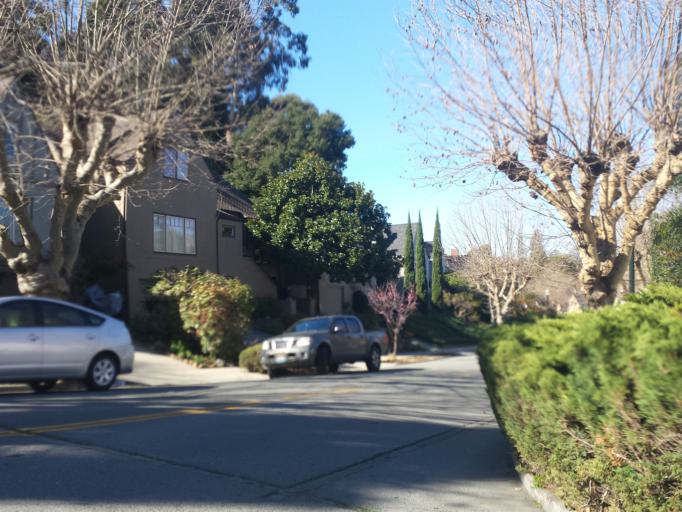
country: US
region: California
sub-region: Alameda County
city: Piedmont
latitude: 37.8061
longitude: -122.2312
